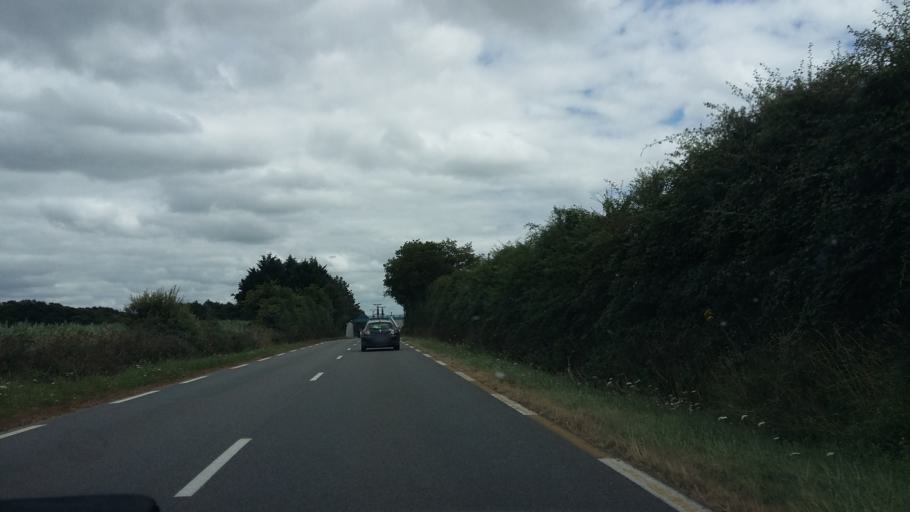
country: FR
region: Pays de la Loire
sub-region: Departement de la Vendee
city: Saint-Christophe-du-Ligneron
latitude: 46.8291
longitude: -1.8038
